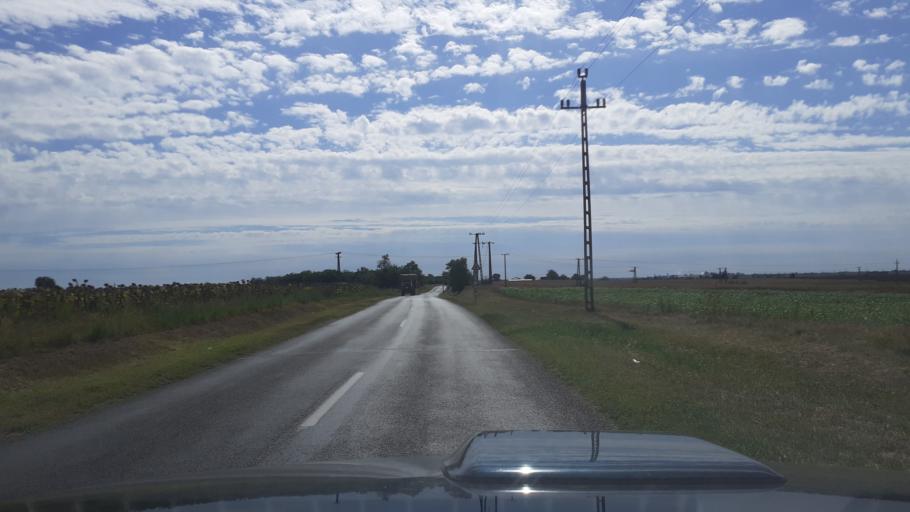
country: HU
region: Fejer
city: Pusztaszabolcs
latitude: 47.1260
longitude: 18.6830
